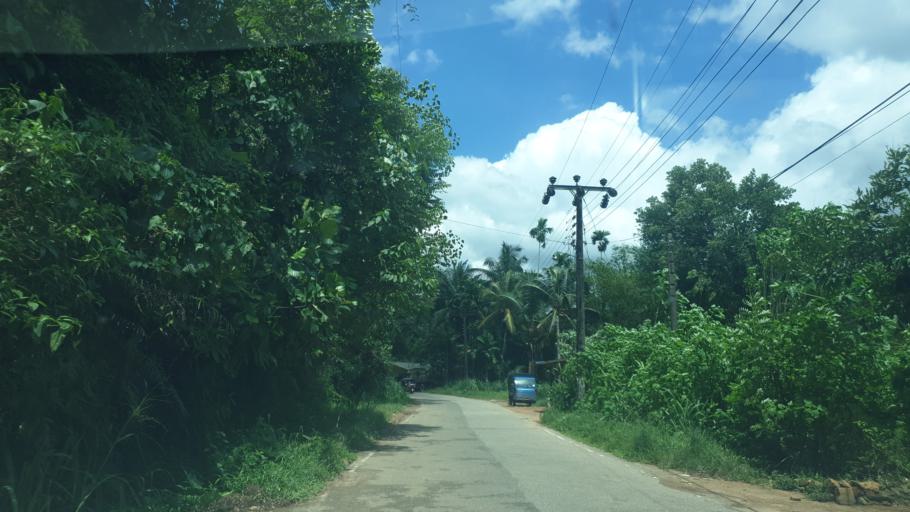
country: LK
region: Sabaragamuwa
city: Ratnapura
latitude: 6.4651
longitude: 80.4293
